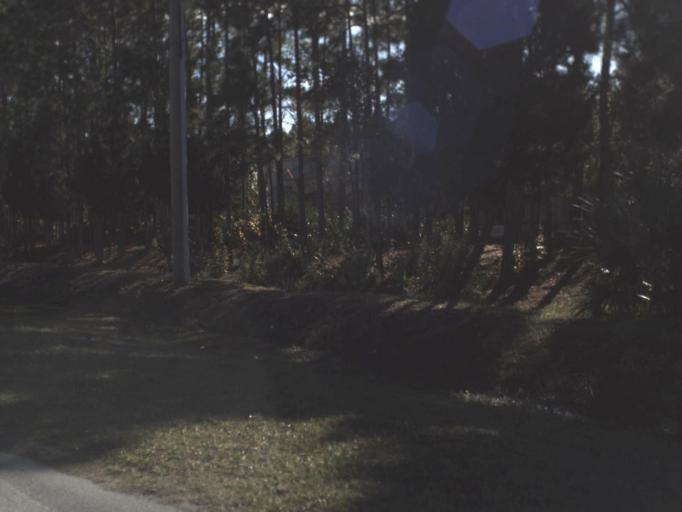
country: US
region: Florida
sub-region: Volusia County
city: Holly Hill
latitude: 29.2148
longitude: -81.0738
